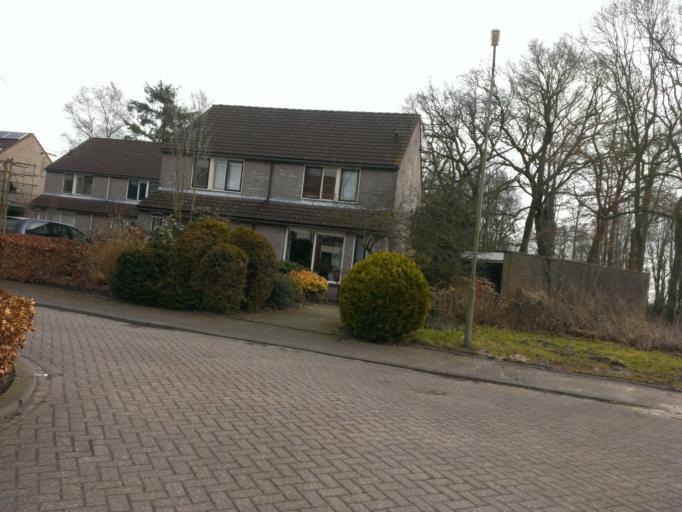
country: NL
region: Gelderland
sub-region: Gemeente Heerde
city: Heerde
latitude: 52.3853
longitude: 6.0467
